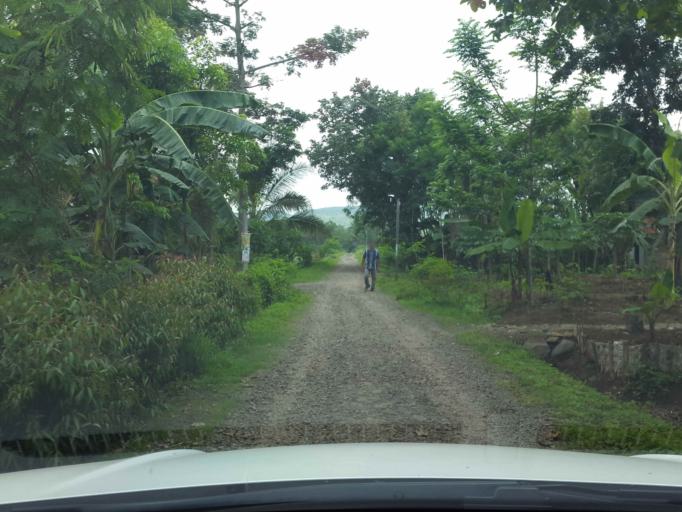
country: ID
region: West Java
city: Cintaratu
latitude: -7.3672
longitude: 108.6859
